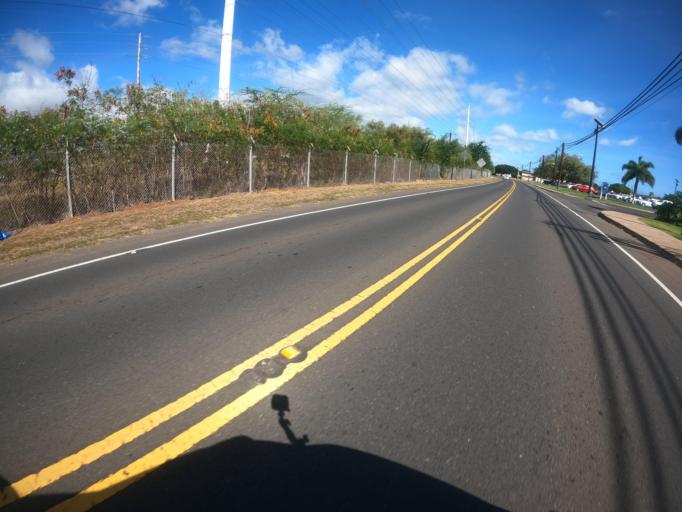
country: US
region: Hawaii
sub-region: Honolulu County
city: Makakilo City
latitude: 21.3229
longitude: -158.0777
